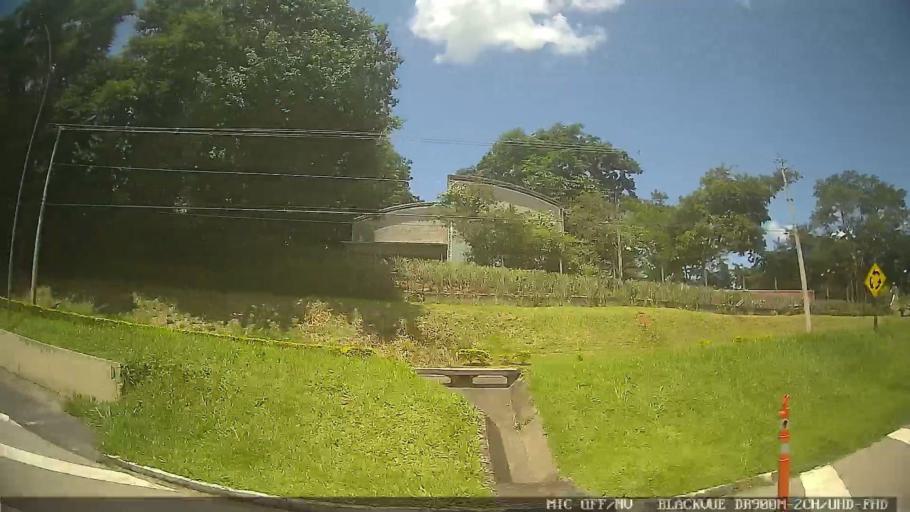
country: BR
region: Sao Paulo
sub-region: Santa Branca
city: Santa Branca
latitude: -23.3198
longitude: -45.7349
